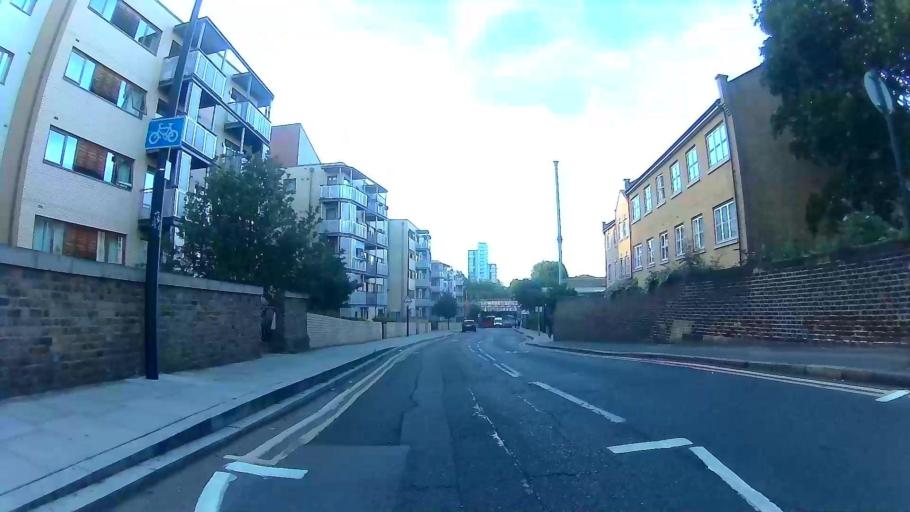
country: GB
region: England
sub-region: Greater London
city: Poplar
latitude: 51.5260
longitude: -0.0203
